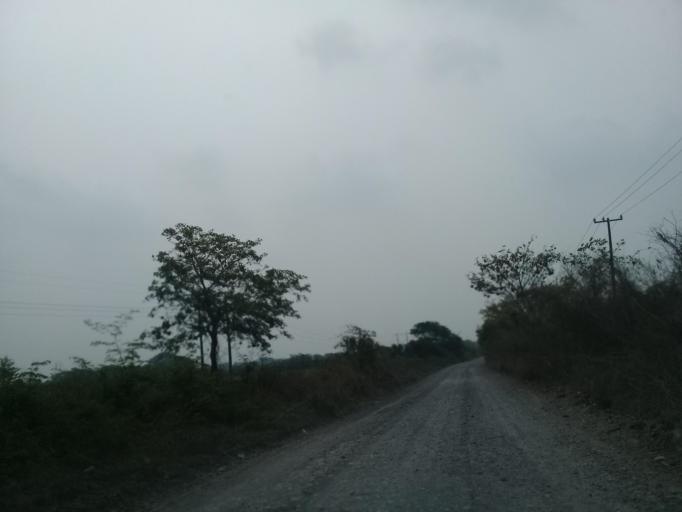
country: MX
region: Veracruz
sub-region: Medellin
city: La Laguna y Monte del Castillo
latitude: 18.9081
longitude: -96.1900
